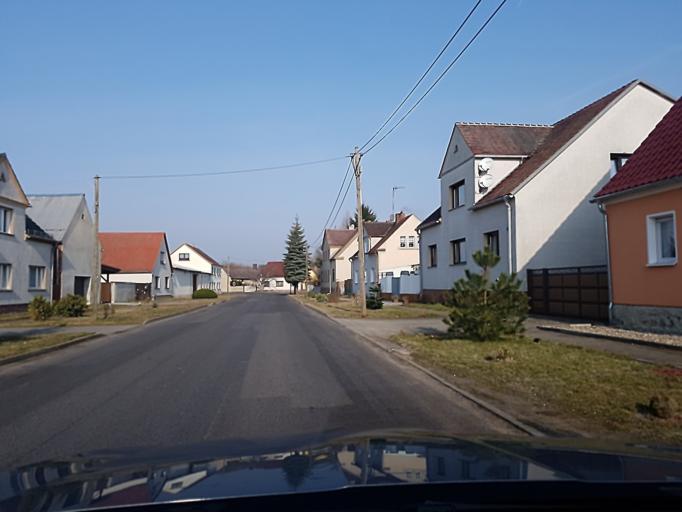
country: DE
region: Brandenburg
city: Falkenberg
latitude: 51.6402
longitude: 13.3012
